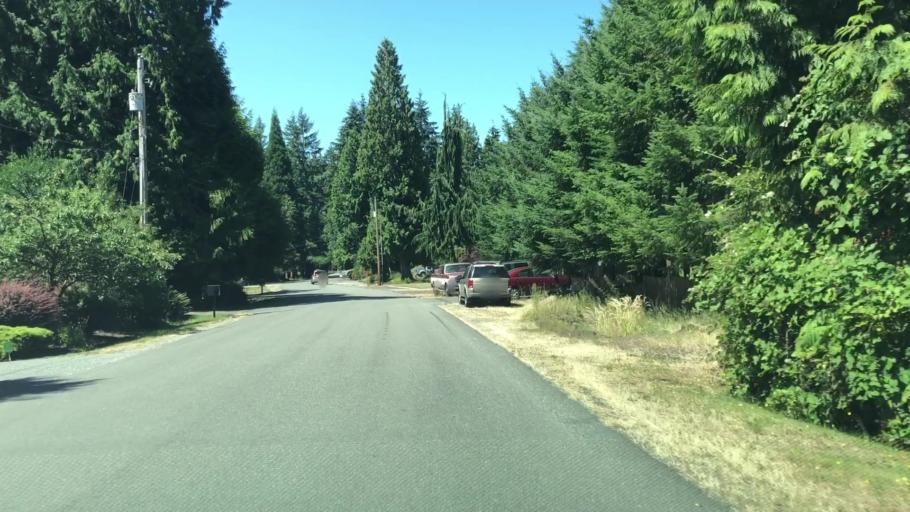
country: US
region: Washington
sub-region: King County
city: Woodinville
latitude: 47.7729
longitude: -122.1331
